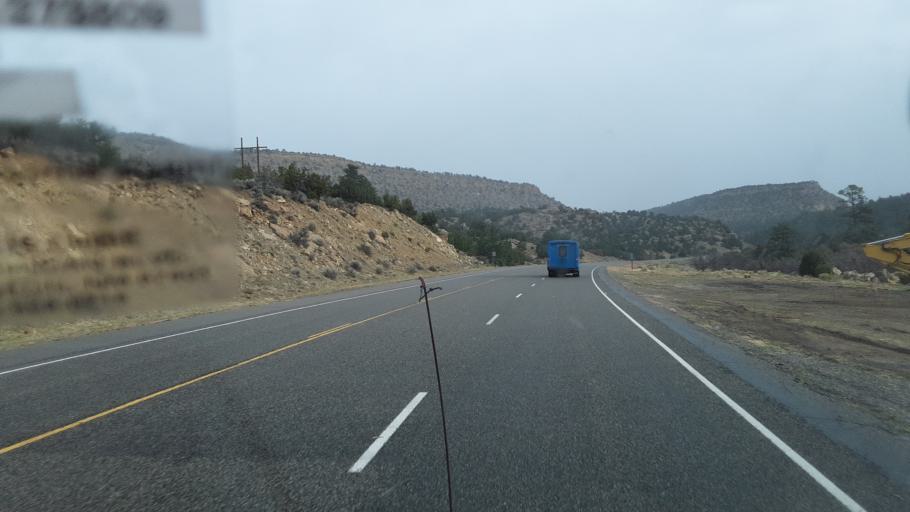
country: US
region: New Mexico
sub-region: Rio Arriba County
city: Tierra Amarilla
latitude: 36.4033
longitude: -106.4936
